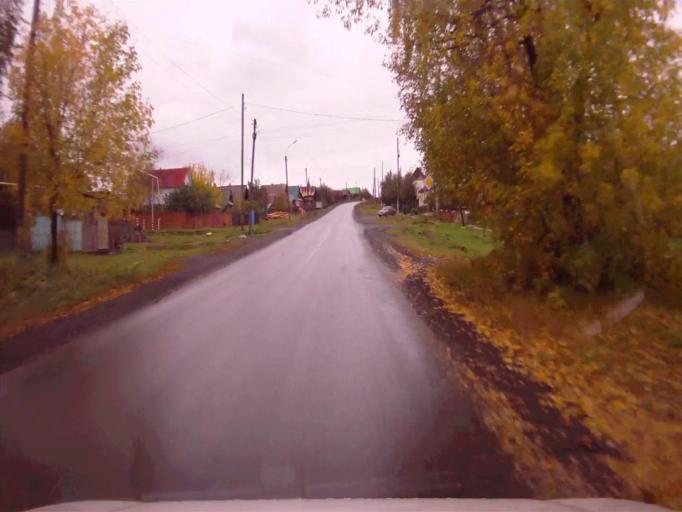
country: RU
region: Chelyabinsk
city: Verkhniy Ufaley
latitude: 56.0504
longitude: 60.2059
